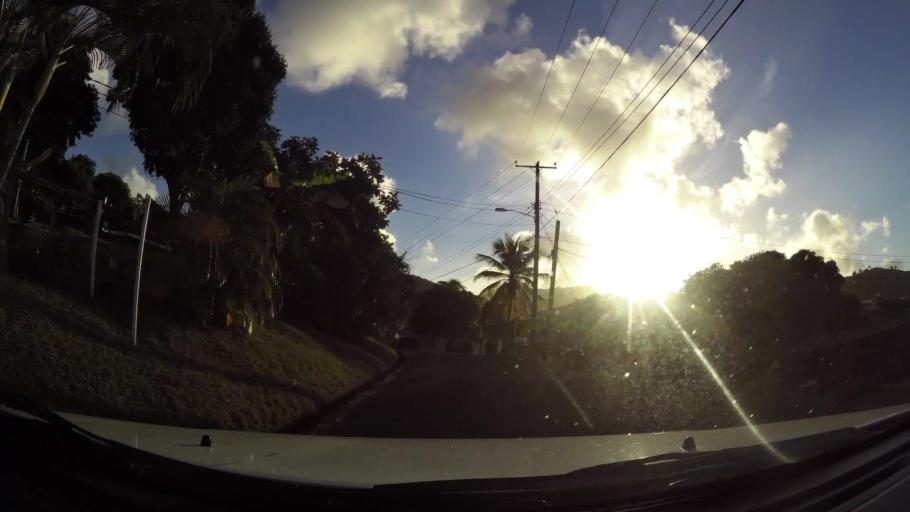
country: LC
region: Gros-Islet
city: Gros Islet
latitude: 14.0631
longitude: -60.9400
